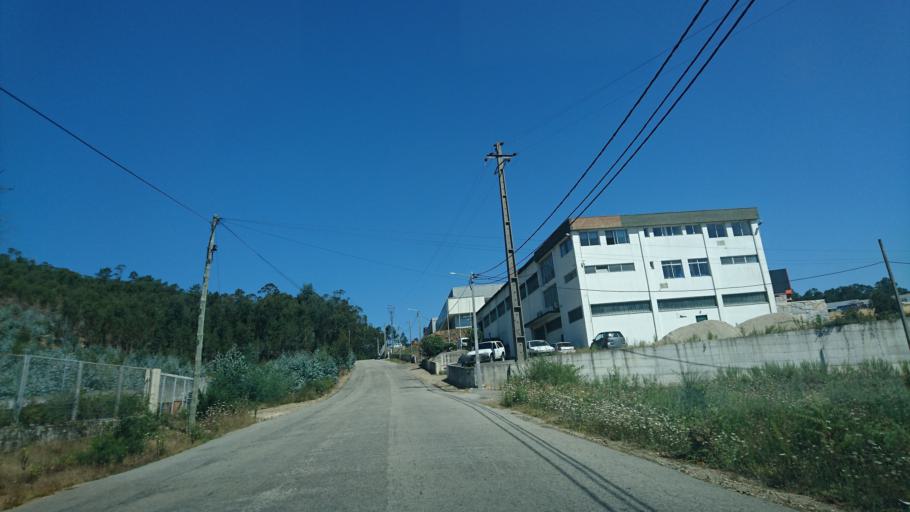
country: PT
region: Aveiro
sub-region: Oliveira de Azemeis
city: Vila Cha
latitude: 40.8819
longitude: -8.4286
